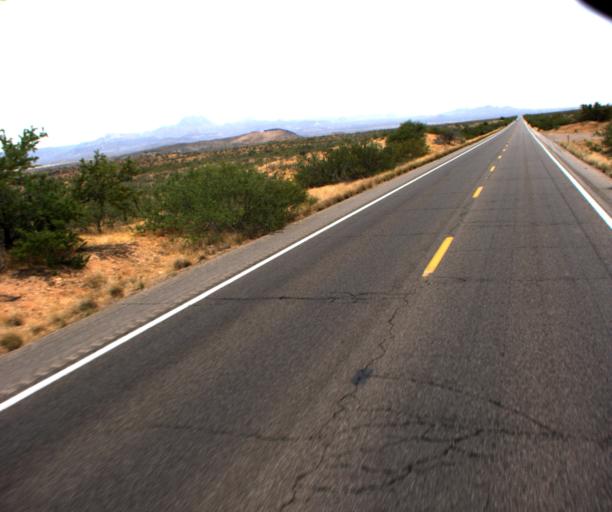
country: US
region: Arizona
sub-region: Gila County
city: Peridot
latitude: 33.3197
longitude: -110.5344
